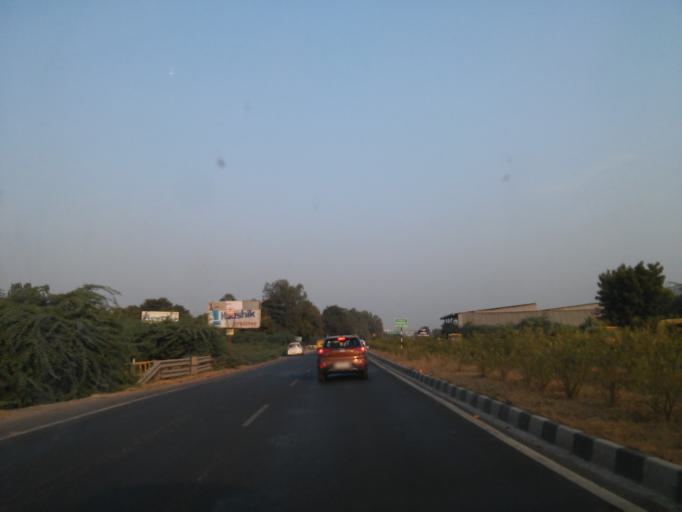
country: IN
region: Gujarat
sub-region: Ahmadabad
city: Sarkhej
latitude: 22.9877
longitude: 72.4507
